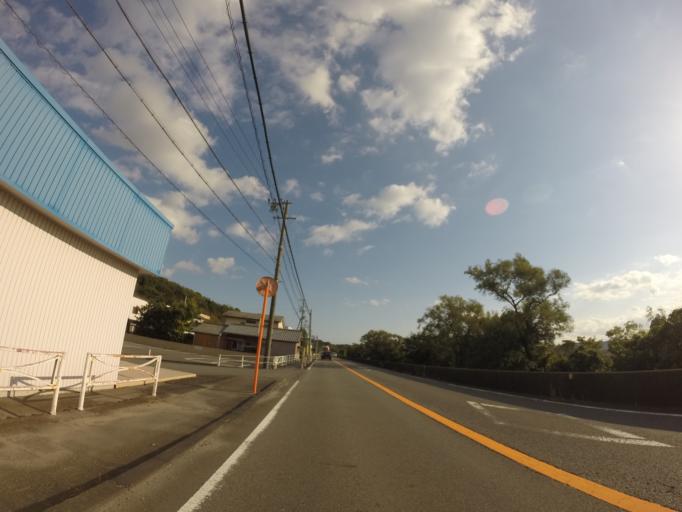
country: JP
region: Shizuoka
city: Kanaya
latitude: 34.8529
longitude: 138.1390
